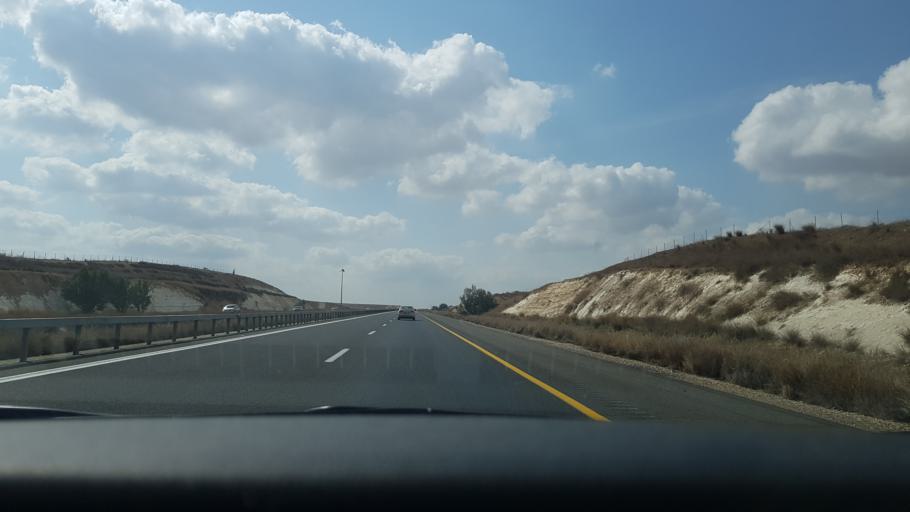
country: IL
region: Southern District
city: Qiryat Gat
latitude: 31.5499
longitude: 34.7997
